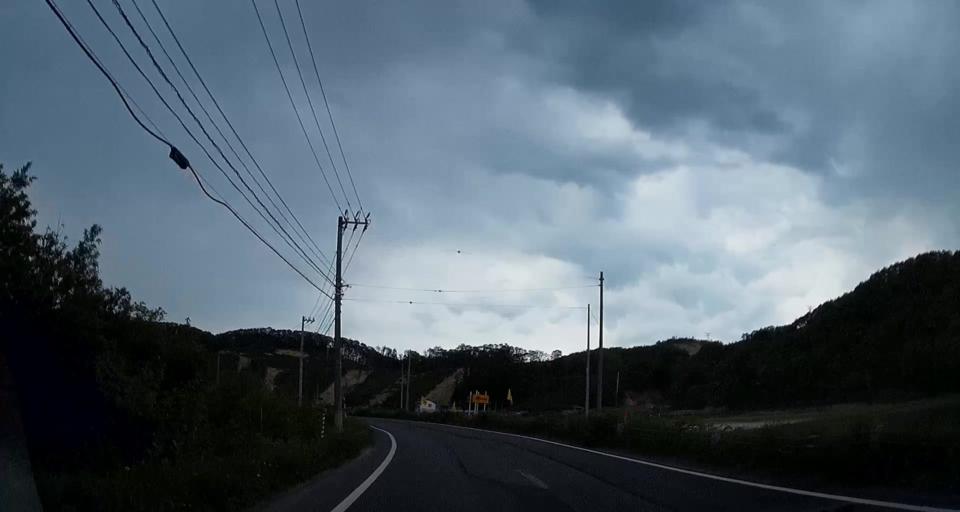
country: JP
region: Hokkaido
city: Chitose
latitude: 42.7583
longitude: 141.9203
